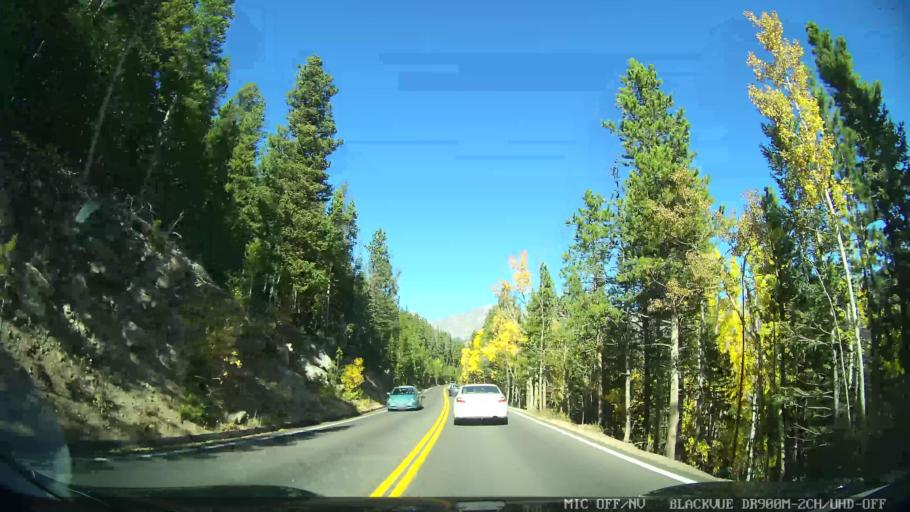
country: US
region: Colorado
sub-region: Larimer County
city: Estes Park
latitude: 40.3948
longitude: -105.6384
